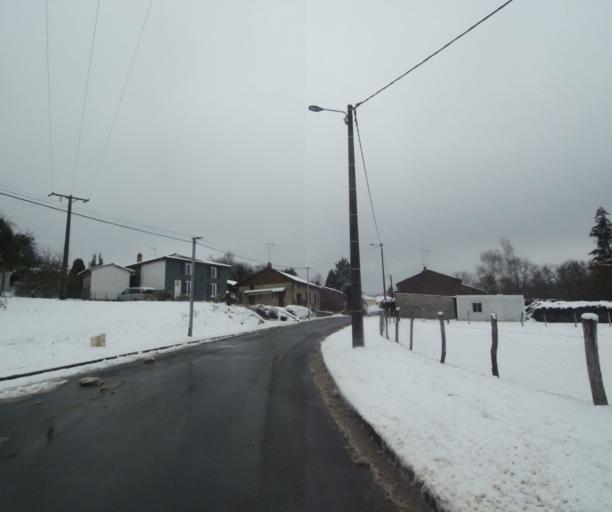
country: FR
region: Champagne-Ardenne
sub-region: Departement de la Haute-Marne
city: Laneuville-a-Remy
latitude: 48.4598
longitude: 4.9149
